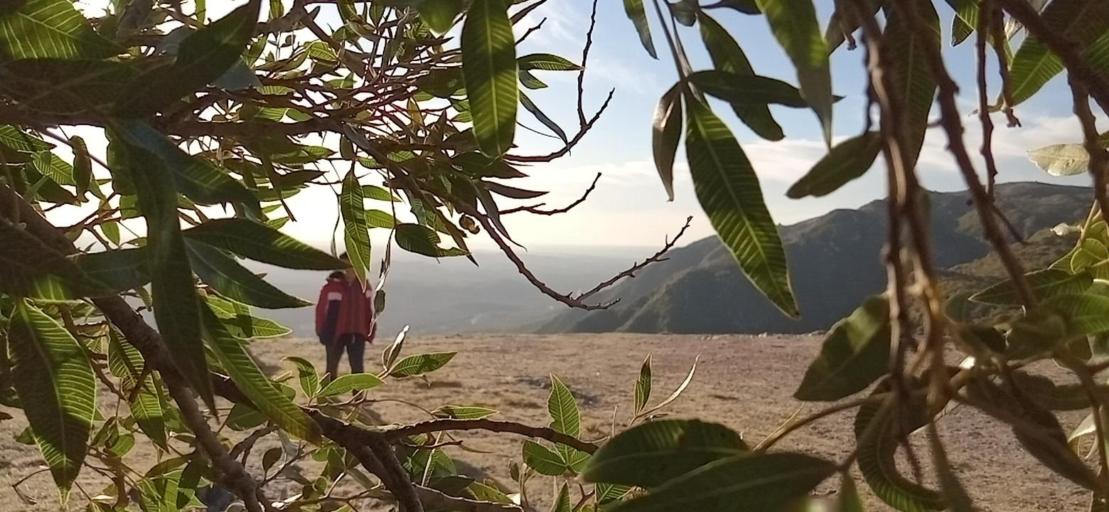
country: AR
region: Cordoba
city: Dolores
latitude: -30.9673
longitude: -64.5848
